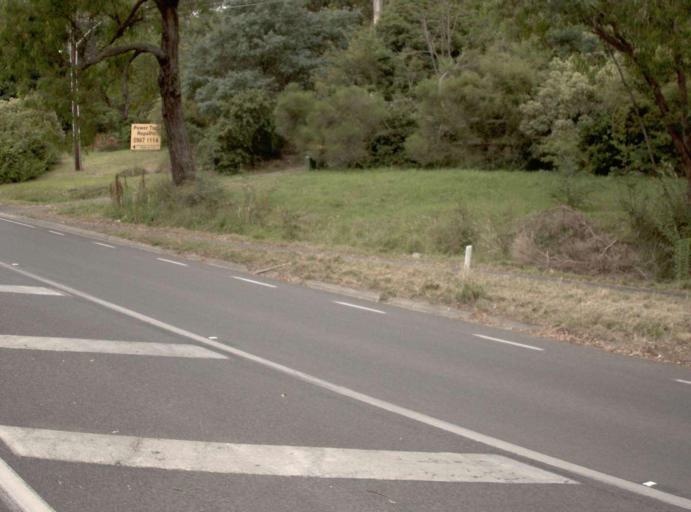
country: AU
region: Victoria
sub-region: Yarra Ranges
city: Yarra Junction
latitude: -37.7773
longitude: 145.6041
